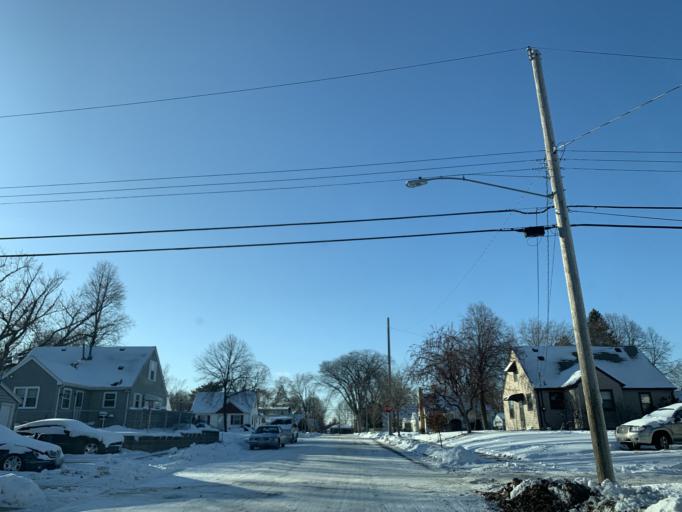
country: US
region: Minnesota
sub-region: Hennepin County
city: Richfield
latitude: 44.9000
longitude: -93.2183
